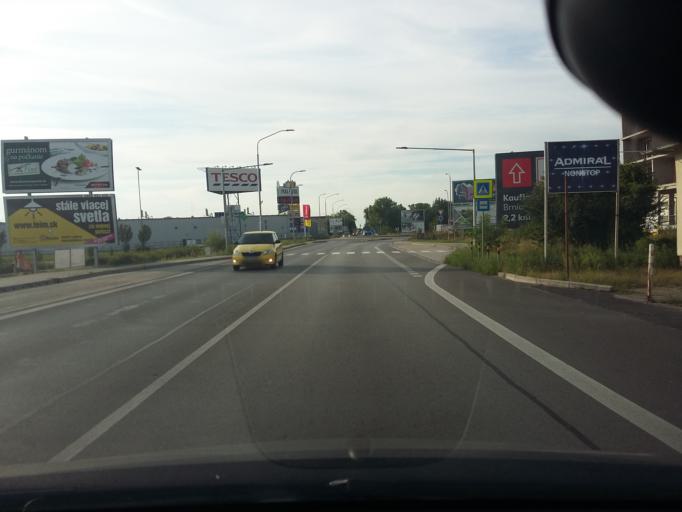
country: SK
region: Bratislavsky
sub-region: Okres Malacky
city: Malacky
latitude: 48.4319
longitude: 17.0309
